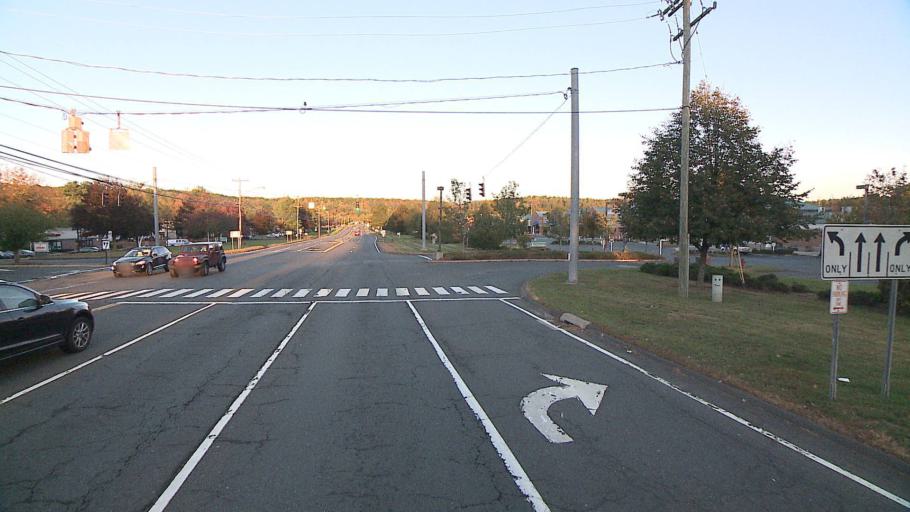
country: US
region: Connecticut
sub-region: Hartford County
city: Canton Valley
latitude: 41.8151
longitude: -72.8605
